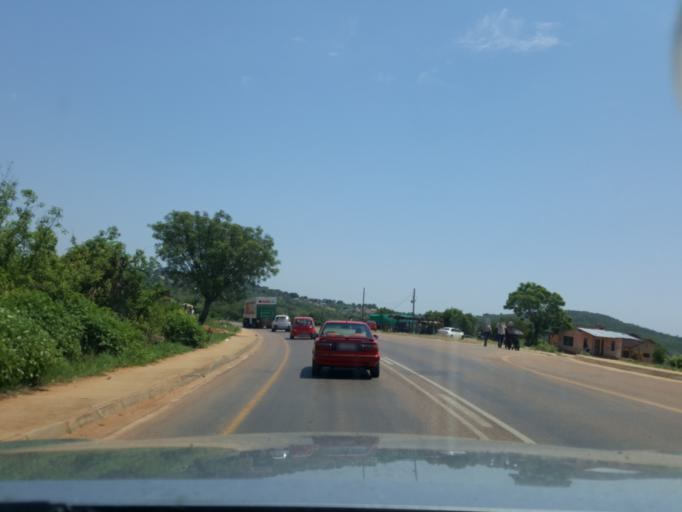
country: ZA
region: Limpopo
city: Thulamahashi
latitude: -24.9544
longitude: 31.1284
